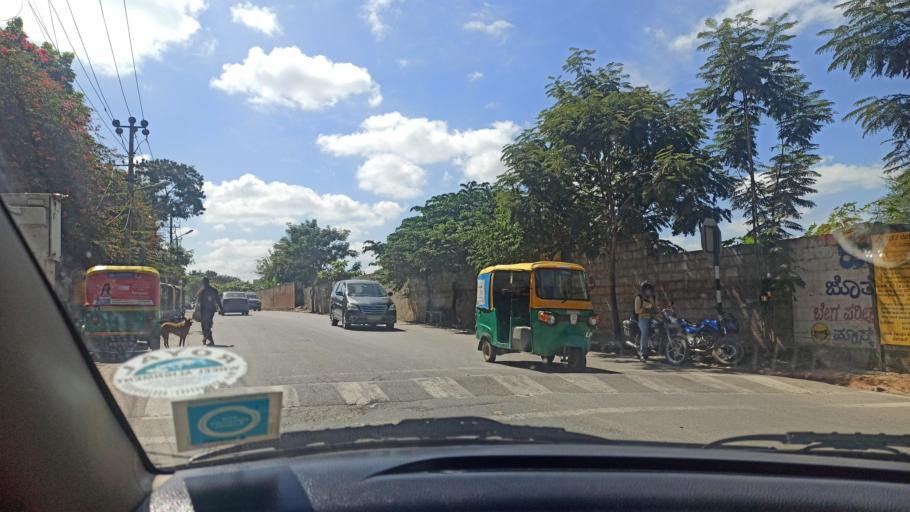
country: IN
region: Karnataka
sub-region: Bangalore Urban
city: Bangalore
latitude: 12.9187
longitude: 77.6688
